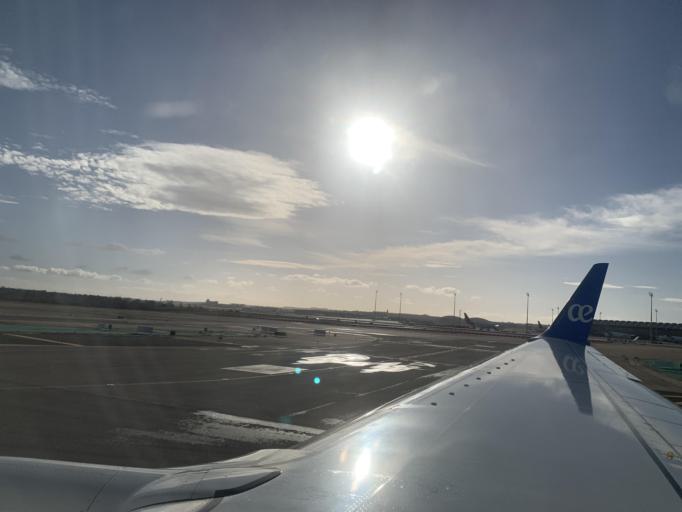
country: ES
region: Madrid
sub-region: Provincia de Madrid
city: Barajas de Madrid
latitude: 40.4953
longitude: -3.5585
